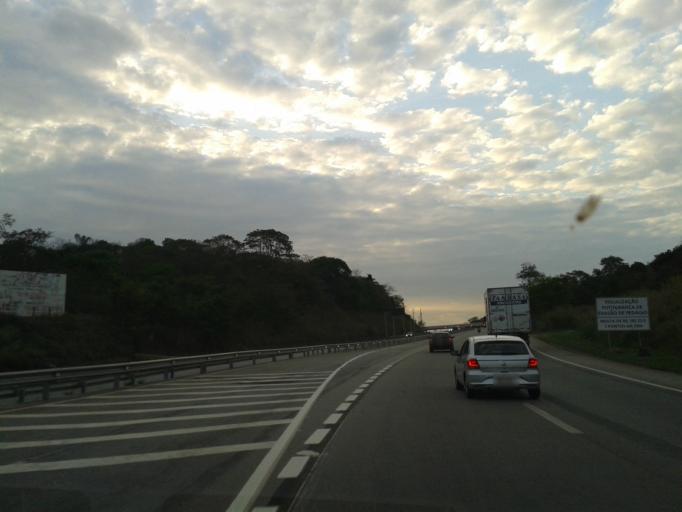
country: BR
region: Minas Gerais
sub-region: Mateus Leme
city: Mateus Leme
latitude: -19.9131
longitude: -44.5024
